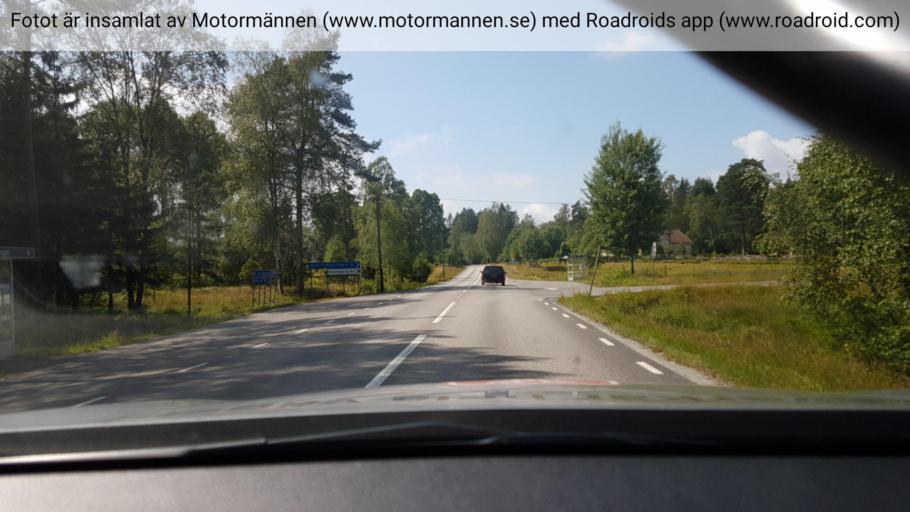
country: SE
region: Vaestra Goetaland
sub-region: Marks Kommun
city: Fritsla
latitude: 57.4786
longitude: 12.7879
